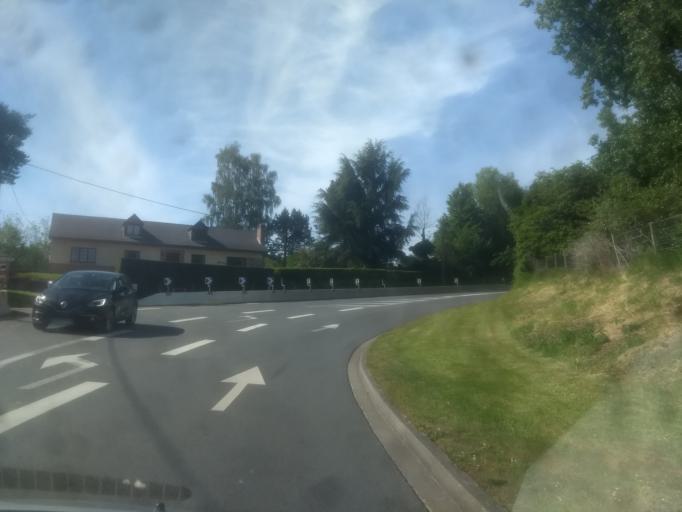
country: FR
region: Picardie
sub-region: Departement de la Somme
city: Doullens
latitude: 50.1622
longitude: 2.3001
